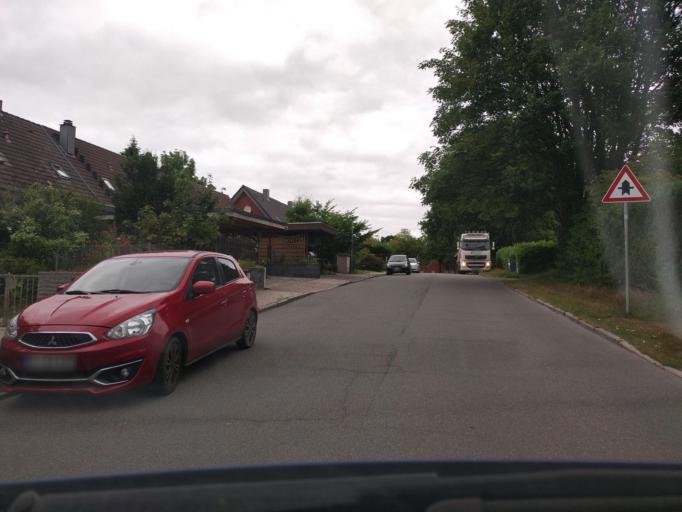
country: DE
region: Schleswig-Holstein
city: Neuberend
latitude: 54.5231
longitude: 9.5276
